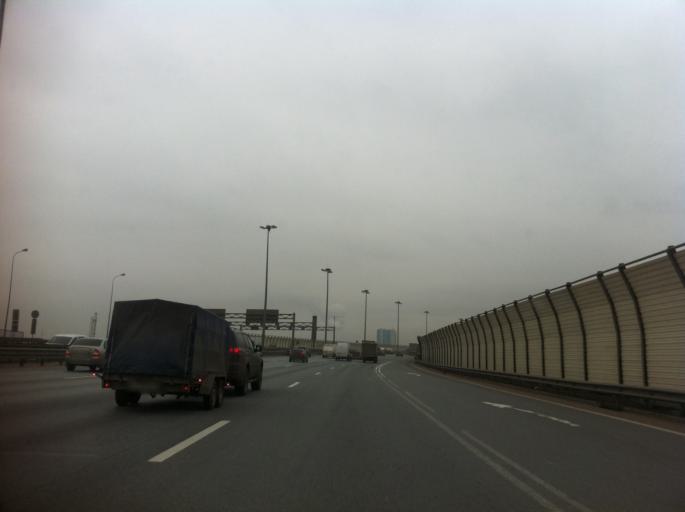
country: RU
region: Leningrad
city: Rybatskoye
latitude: 59.8564
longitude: 30.5097
